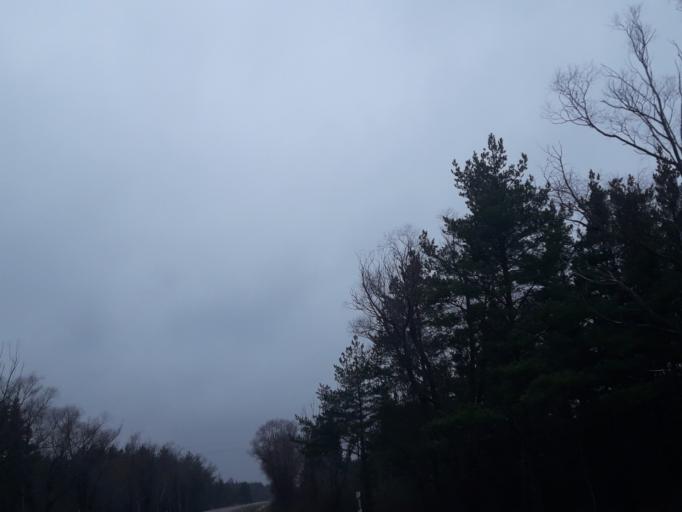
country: EE
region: Saare
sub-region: Kuressaare linn
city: Kuressaare
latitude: 58.2756
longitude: 22.4472
